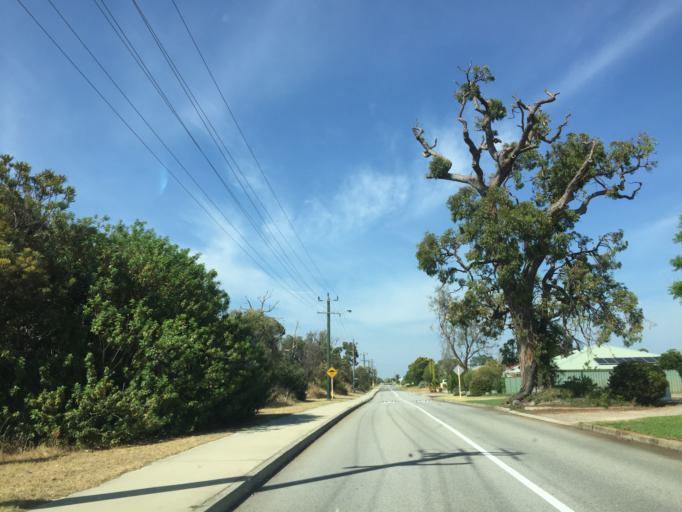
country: AU
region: Western Australia
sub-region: Gosnells
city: Thornlie
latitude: -32.0821
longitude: 115.9604
